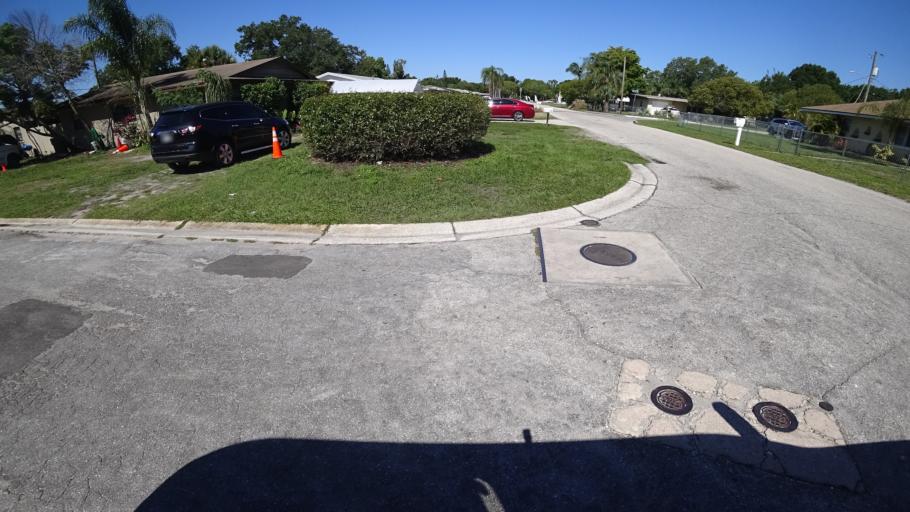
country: US
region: Florida
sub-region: Manatee County
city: West Bradenton
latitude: 27.4865
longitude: -82.5958
